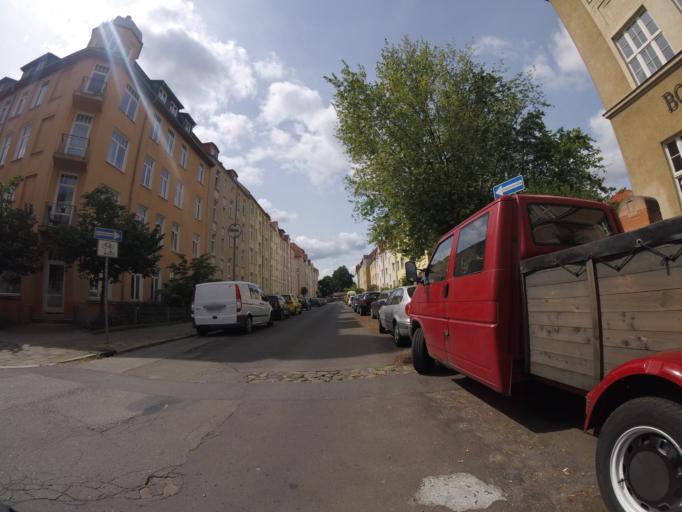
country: DE
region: Mecklenburg-Vorpommern
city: Rostock
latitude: 54.0905
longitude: 12.1108
